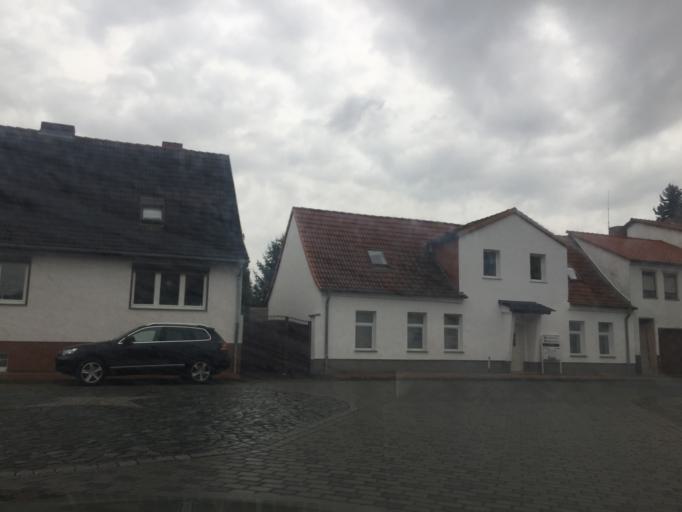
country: DE
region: Saxony-Anhalt
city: Egeln
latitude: 51.9412
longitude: 11.4300
